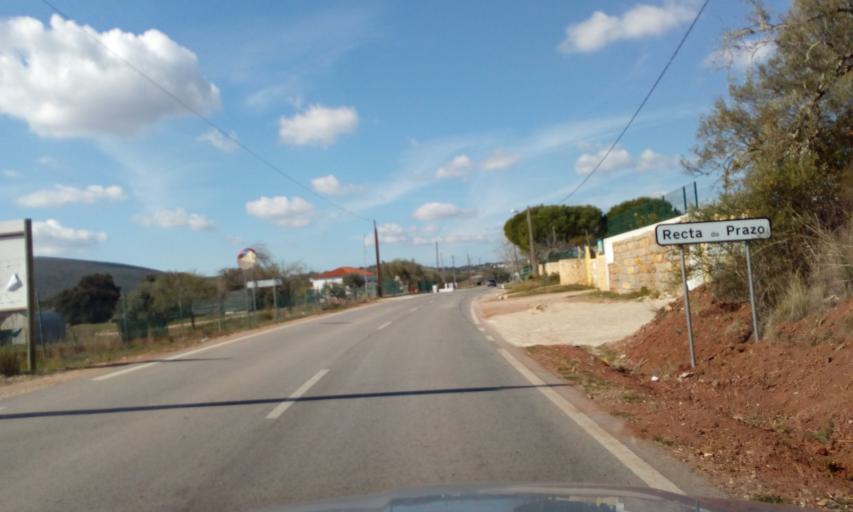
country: PT
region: Faro
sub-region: Loule
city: Loule
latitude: 37.2443
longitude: -8.0512
